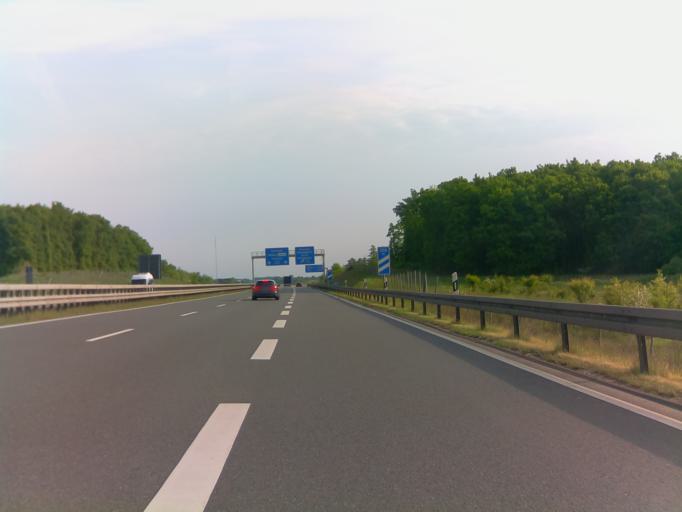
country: DE
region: Lower Saxony
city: Lehre
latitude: 52.3004
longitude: 10.7231
